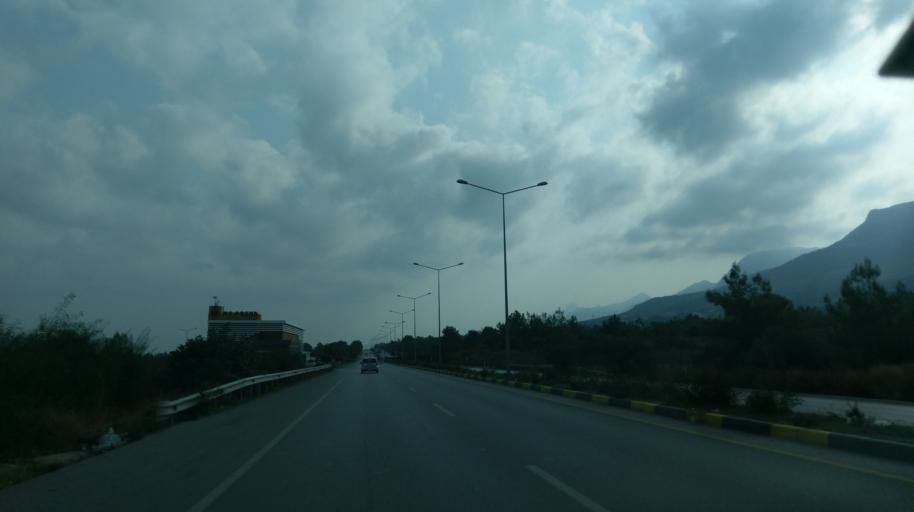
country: CY
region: Keryneia
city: Kyrenia
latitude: 35.3290
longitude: 33.2843
